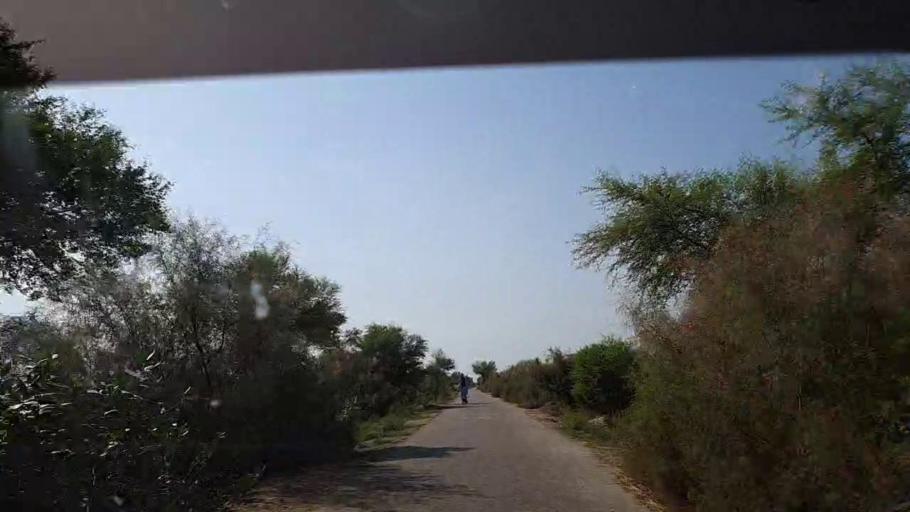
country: PK
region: Sindh
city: Ghauspur
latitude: 28.2044
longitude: 69.0353
